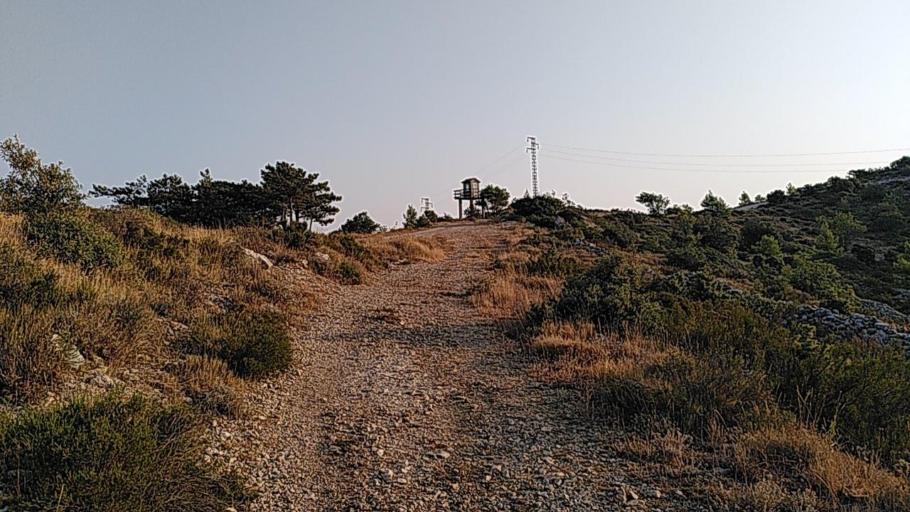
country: HR
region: Splitsko-Dalmatinska
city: Jelsa
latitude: 43.1346
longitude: 16.6802
